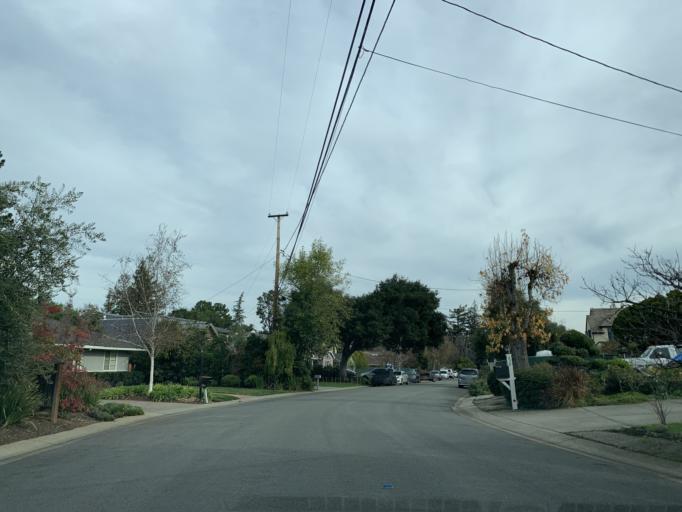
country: US
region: California
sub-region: Santa Clara County
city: Los Altos
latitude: 37.3754
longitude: -122.0991
